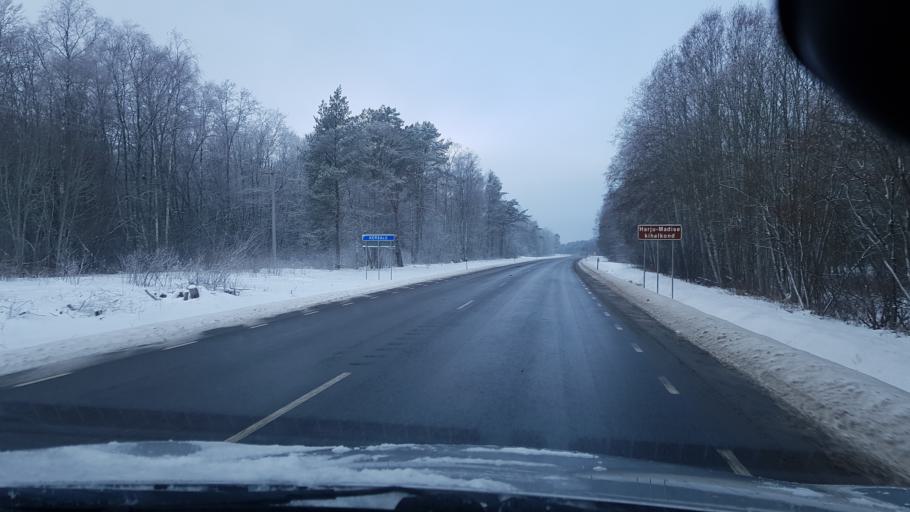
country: EE
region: Harju
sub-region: Paldiski linn
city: Paldiski
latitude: 59.3378
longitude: 24.2247
